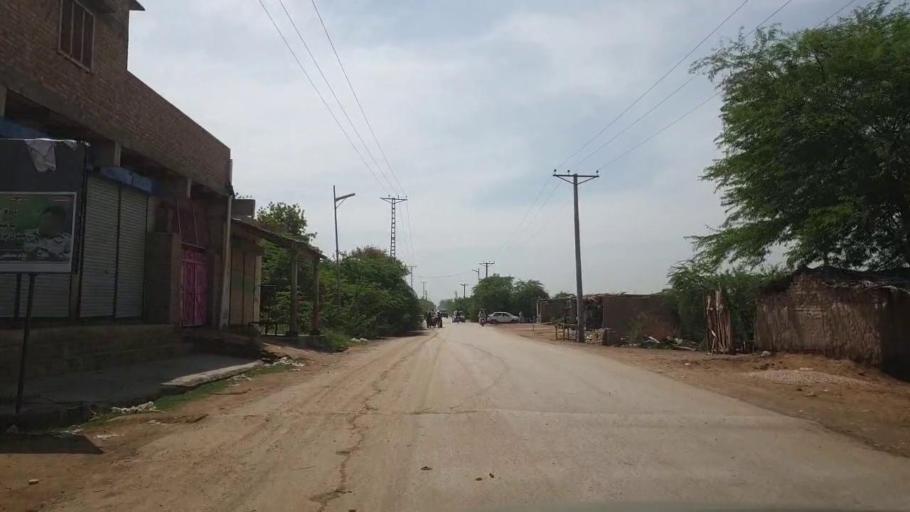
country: PK
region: Sindh
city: Kot Diji
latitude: 27.1612
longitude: 68.9567
